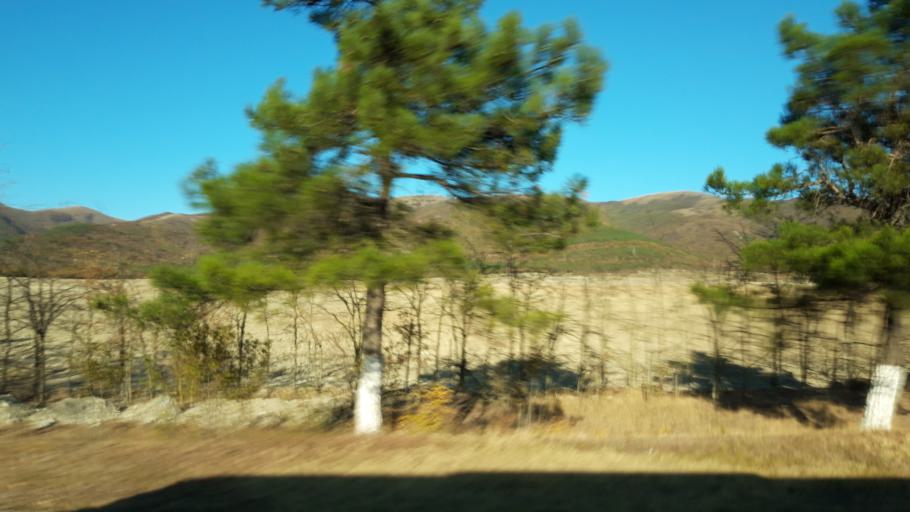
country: RU
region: Krasnodarskiy
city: Kabardinka
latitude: 44.6322
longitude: 38.0007
